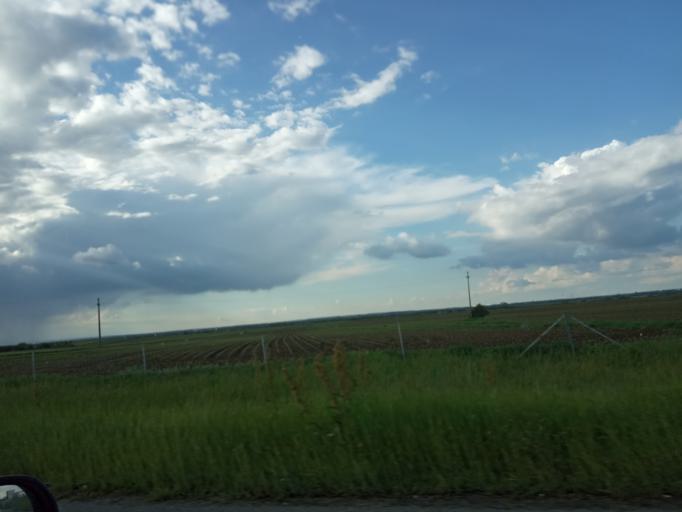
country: RS
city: Dobanovci
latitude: 44.8357
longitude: 20.2617
